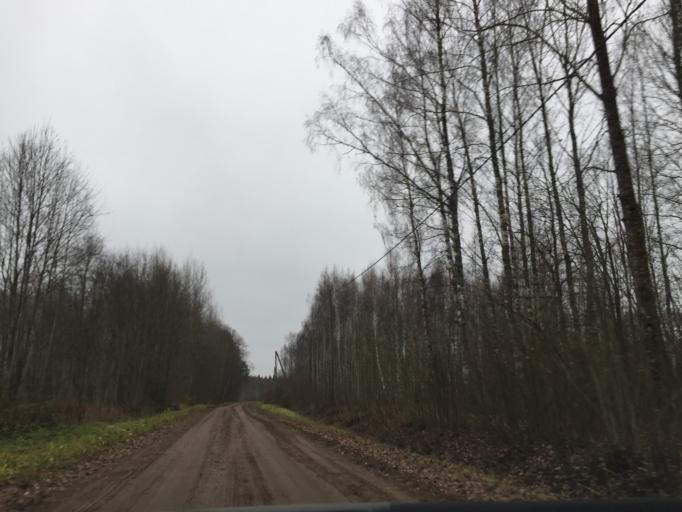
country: LV
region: Limbazu Rajons
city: Limbazi
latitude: 57.5017
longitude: 24.7665
